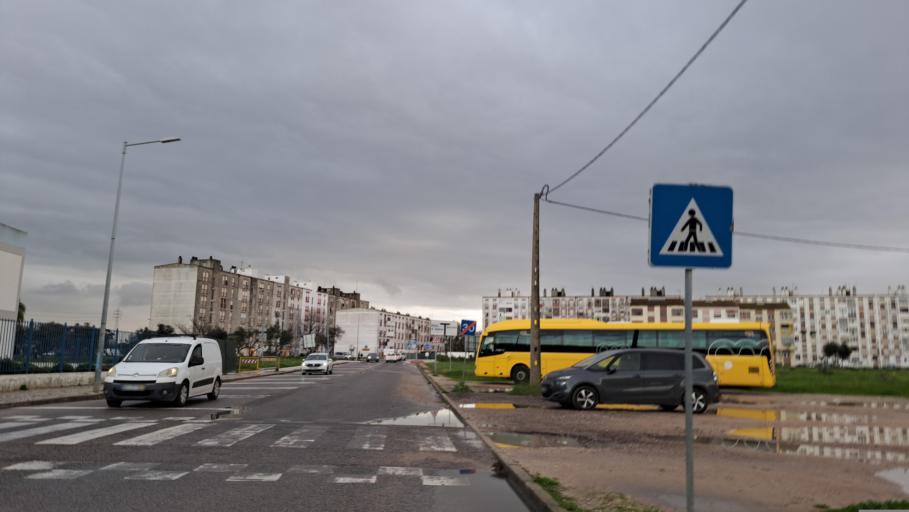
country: PT
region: Setubal
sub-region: Moita
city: Alhos Vedros
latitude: 38.6533
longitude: -9.0376
